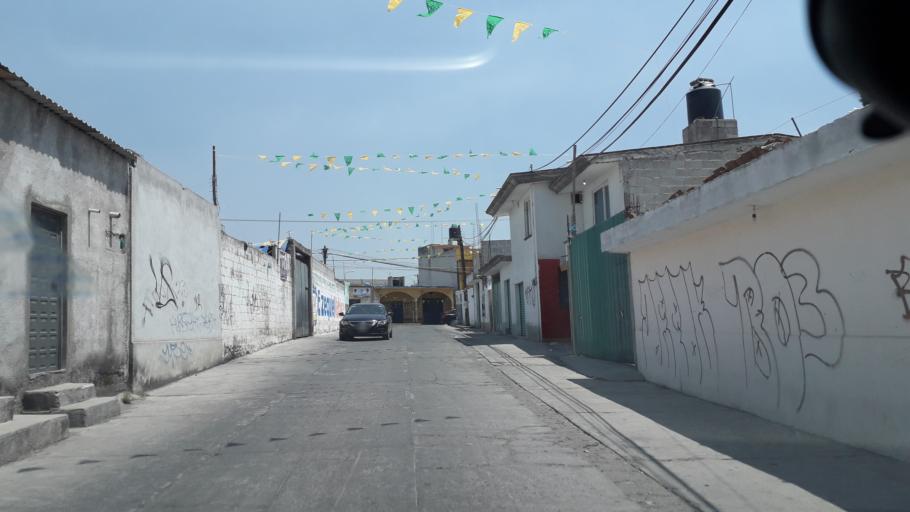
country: MX
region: Puebla
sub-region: Puebla
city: Santa Maria Xonacatepec
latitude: 19.0842
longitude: -98.1072
